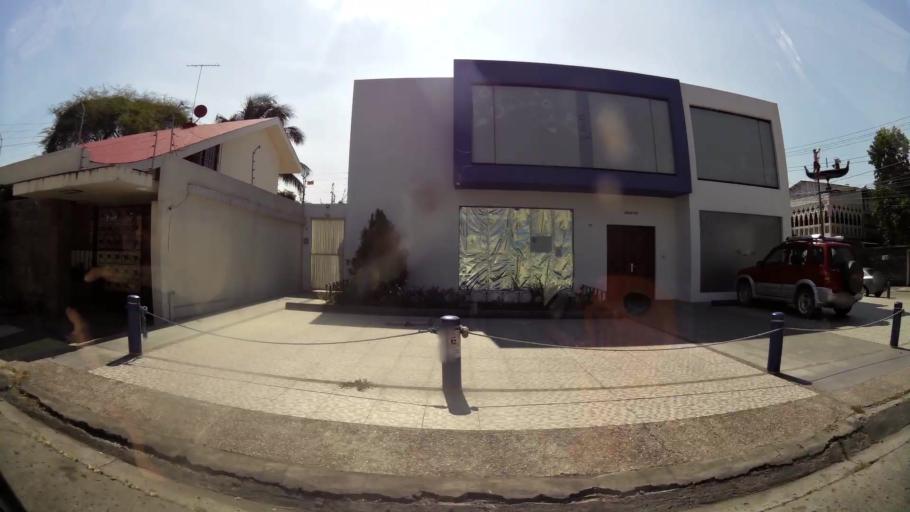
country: EC
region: Guayas
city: Guayaquil
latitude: -2.1716
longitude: -79.9096
